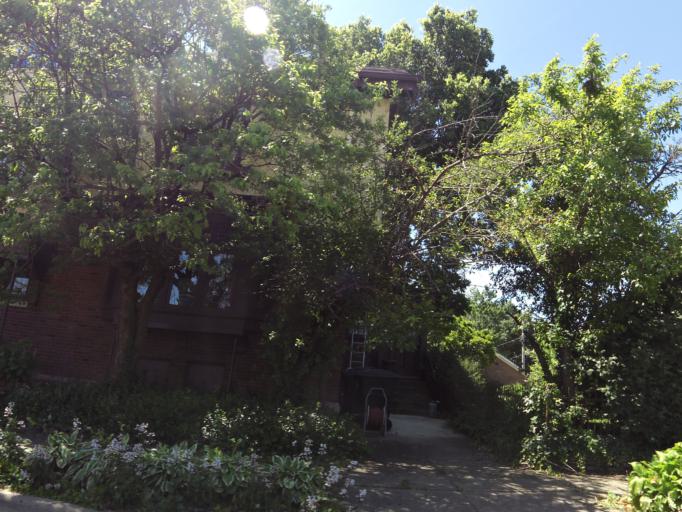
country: US
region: Illinois
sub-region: Vermilion County
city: Danville
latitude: 40.1457
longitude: -87.6307
